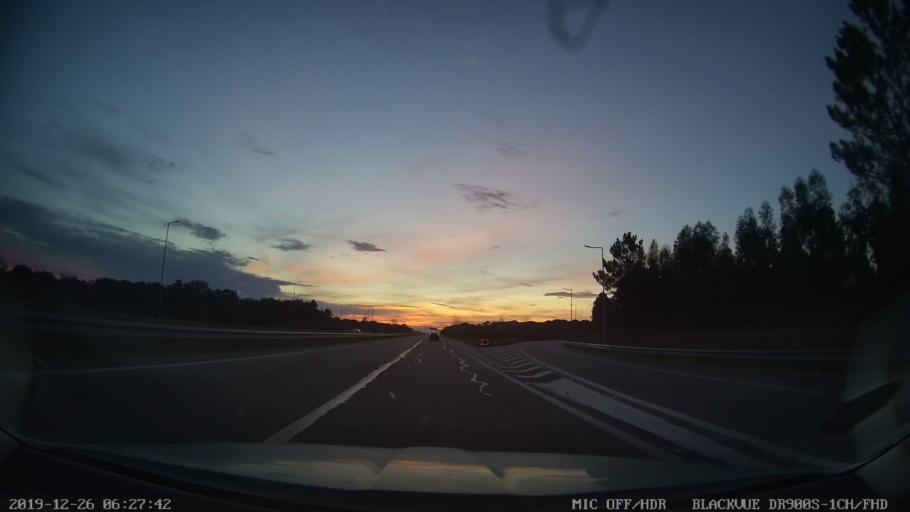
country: PT
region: Evora
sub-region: Vendas Novas
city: Vendas Novas
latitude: 38.6094
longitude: -8.6336
